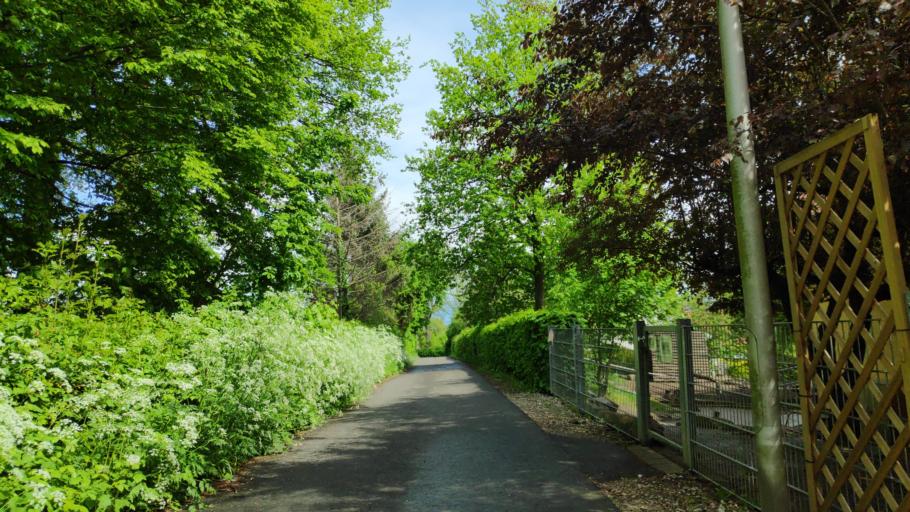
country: DE
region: North Rhine-Westphalia
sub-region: Regierungsbezirk Detmold
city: Minden
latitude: 52.2683
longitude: 8.8885
